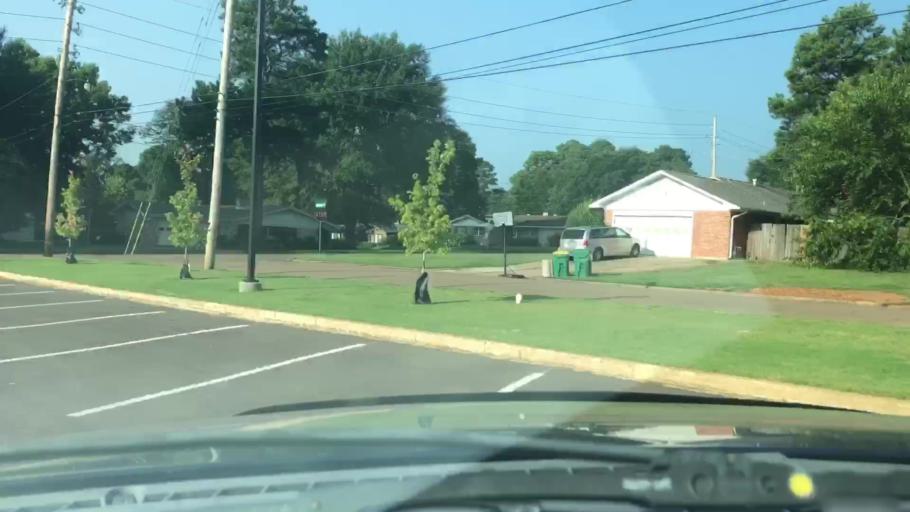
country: US
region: Arkansas
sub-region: Miller County
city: Texarkana
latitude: 33.4612
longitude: -94.0602
